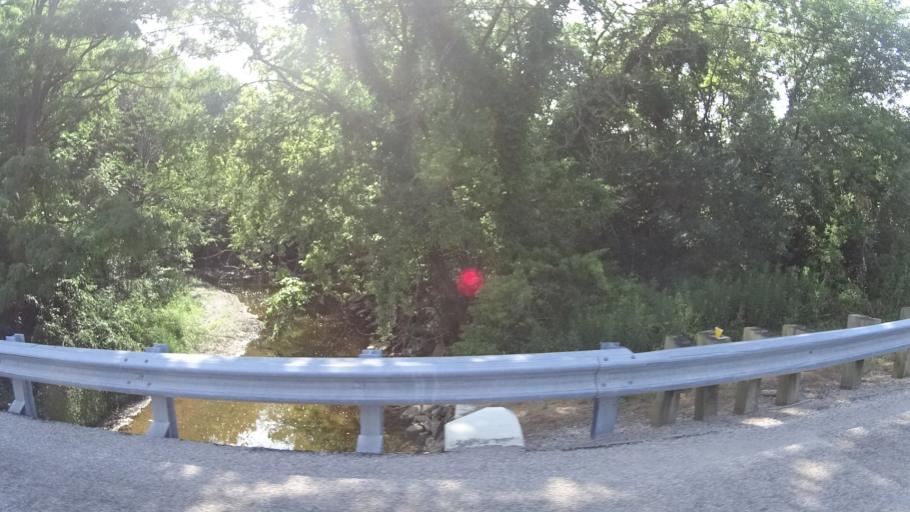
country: US
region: Ohio
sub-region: Lorain County
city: Vermilion
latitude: 41.3809
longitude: -82.4308
